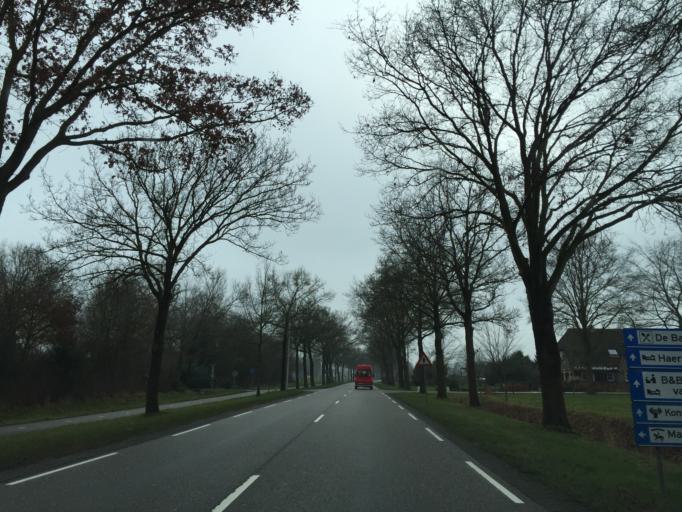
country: NL
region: Overijssel
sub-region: Gemeente Dalfsen
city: Dalfsen
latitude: 52.5257
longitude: 6.2606
